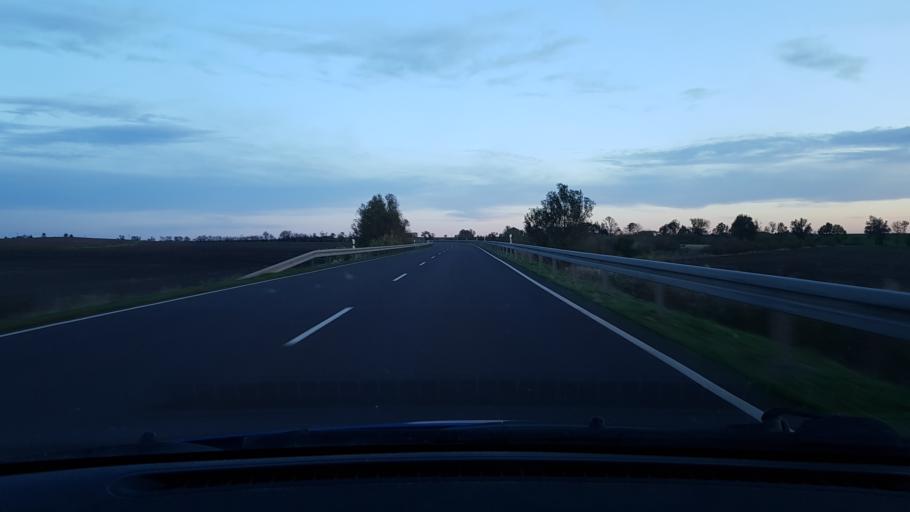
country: DE
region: Saxony-Anhalt
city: Leitzkau
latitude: 52.0565
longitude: 11.9385
